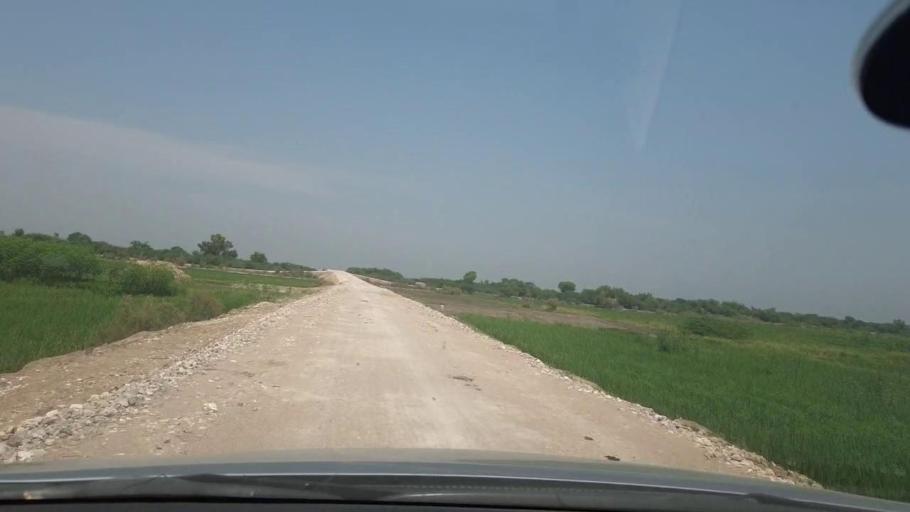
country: PK
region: Balochistan
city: Garhi Khairo
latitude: 28.0607
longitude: 67.9987
